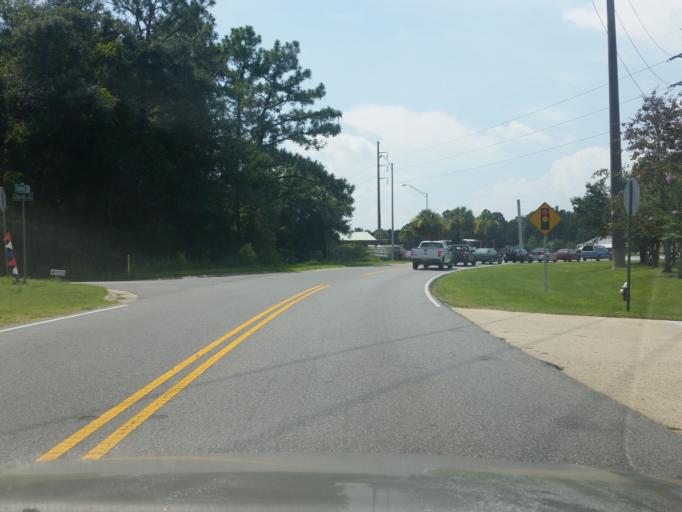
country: US
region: Florida
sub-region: Escambia County
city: Ferry Pass
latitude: 30.5311
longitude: -87.2134
